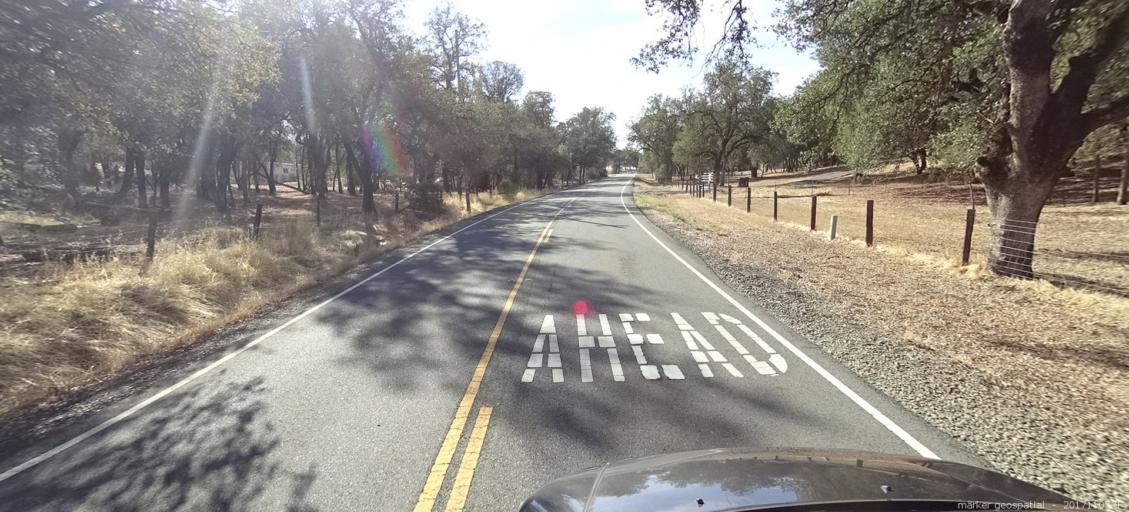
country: US
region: California
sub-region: Shasta County
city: Shasta
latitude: 40.4919
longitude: -122.5489
